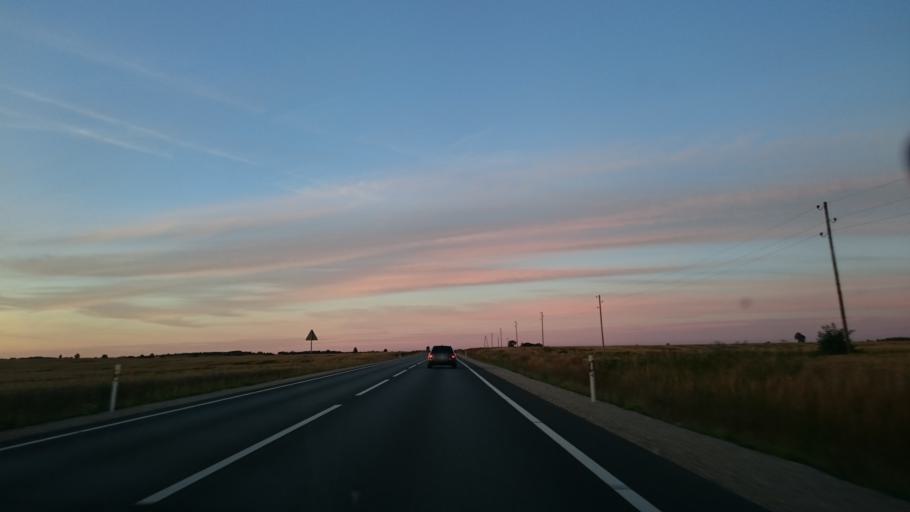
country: LV
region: Dobeles Rajons
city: Dobele
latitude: 56.7267
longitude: 23.2072
